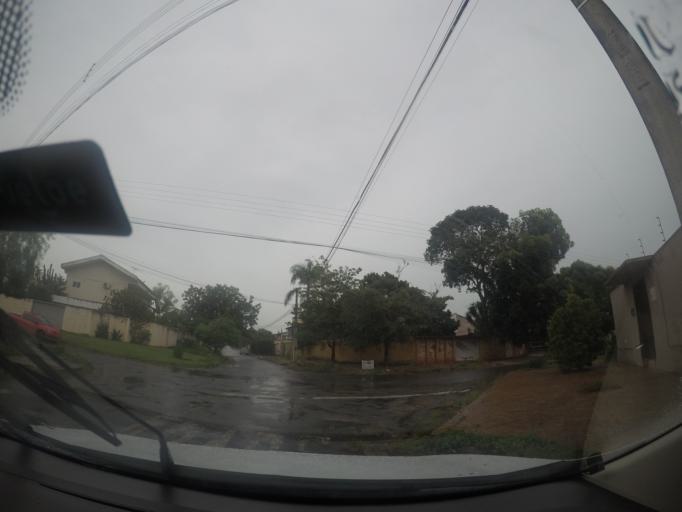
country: BR
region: Goias
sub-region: Goiania
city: Goiania
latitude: -16.6480
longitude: -49.2267
